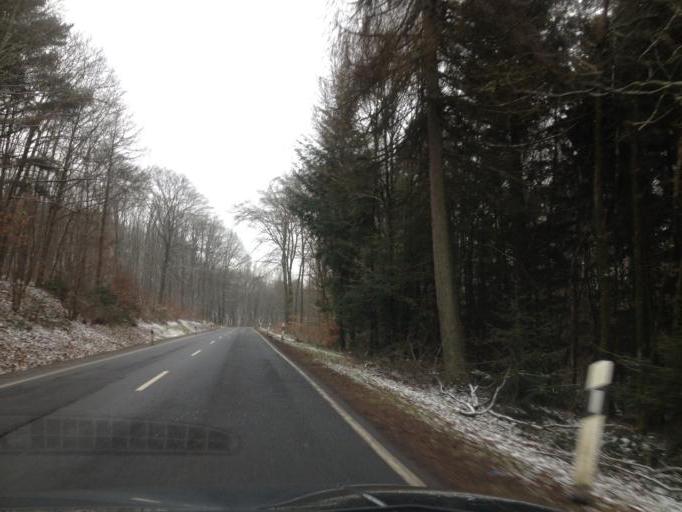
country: DE
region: Rheinland-Pfalz
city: Breitenbach
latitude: 49.3912
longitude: 7.2542
